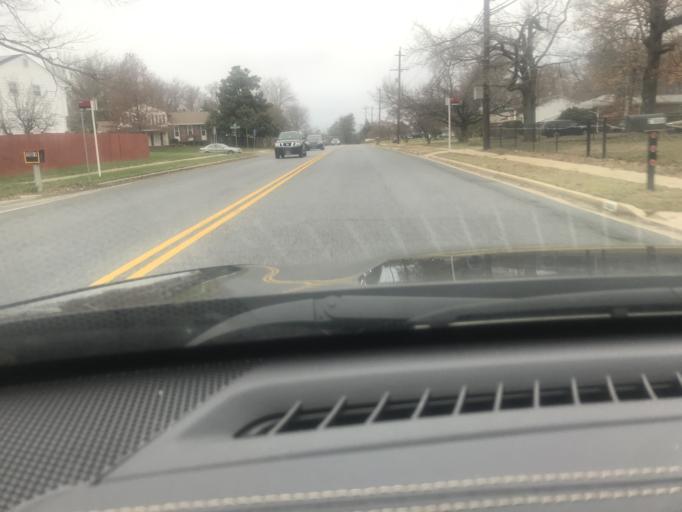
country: US
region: Maryland
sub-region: Prince George's County
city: Oxon Hill
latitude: 38.7826
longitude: -76.9654
